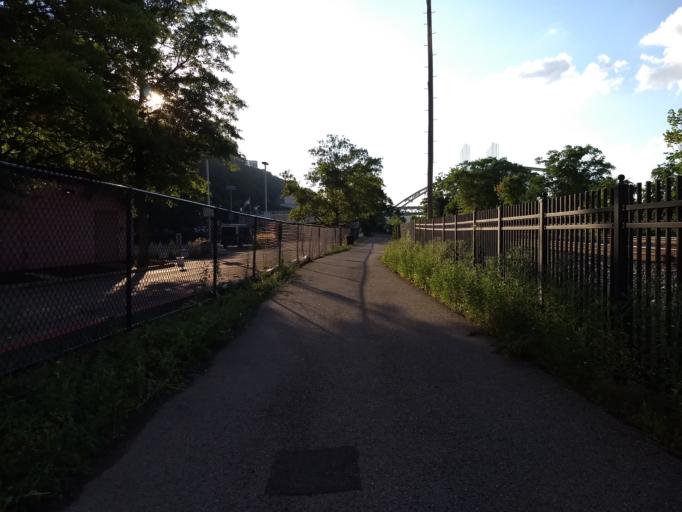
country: US
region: Pennsylvania
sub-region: Allegheny County
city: Pittsburgh
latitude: 40.4354
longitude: -80.0066
